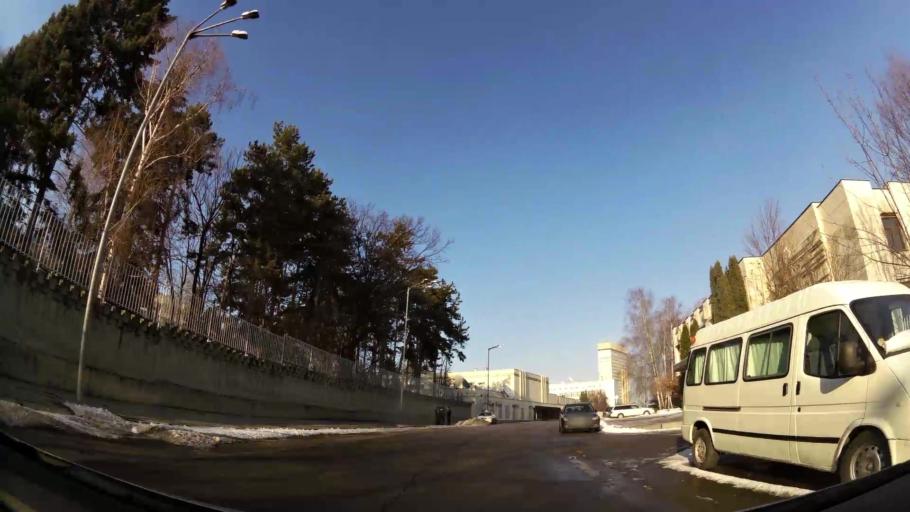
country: BG
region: Sofia-Capital
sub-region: Stolichna Obshtina
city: Sofia
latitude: 42.6708
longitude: 23.3458
